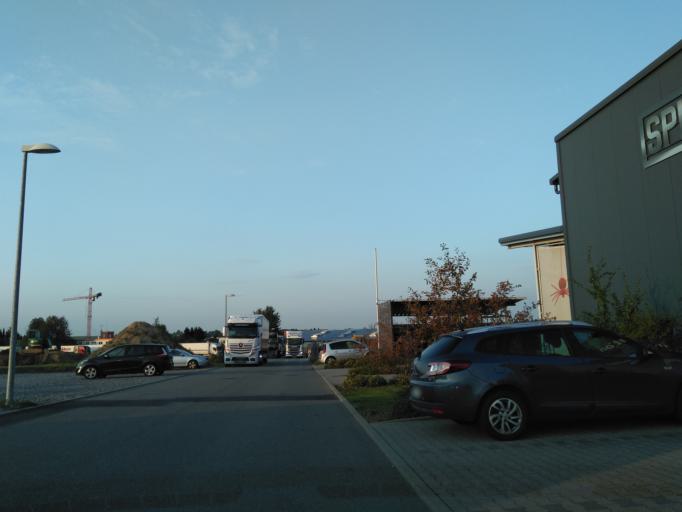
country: DE
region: Baden-Wuerttemberg
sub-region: Regierungsbezirk Stuttgart
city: Markgroningen
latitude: 48.8987
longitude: 9.0999
